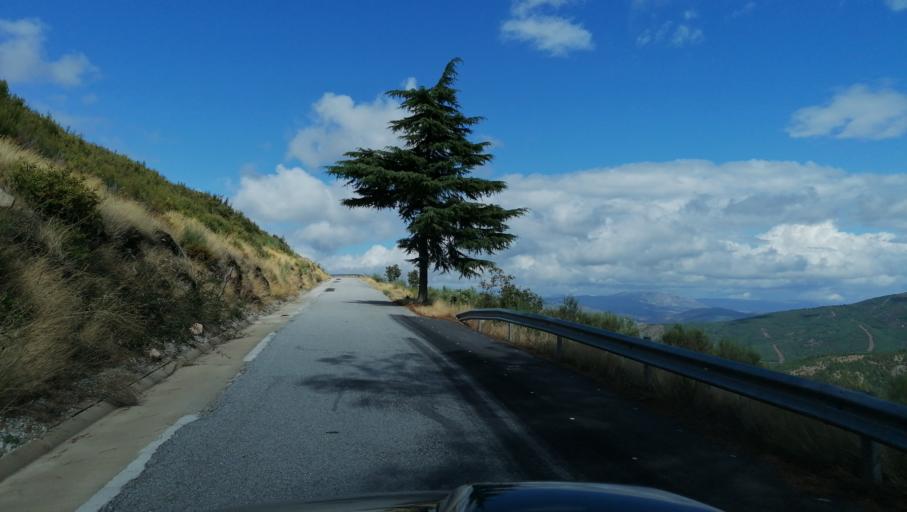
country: PT
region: Vila Real
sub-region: Vila Pouca de Aguiar
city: Vila Pouca de Aguiar
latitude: 41.5582
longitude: -7.6793
